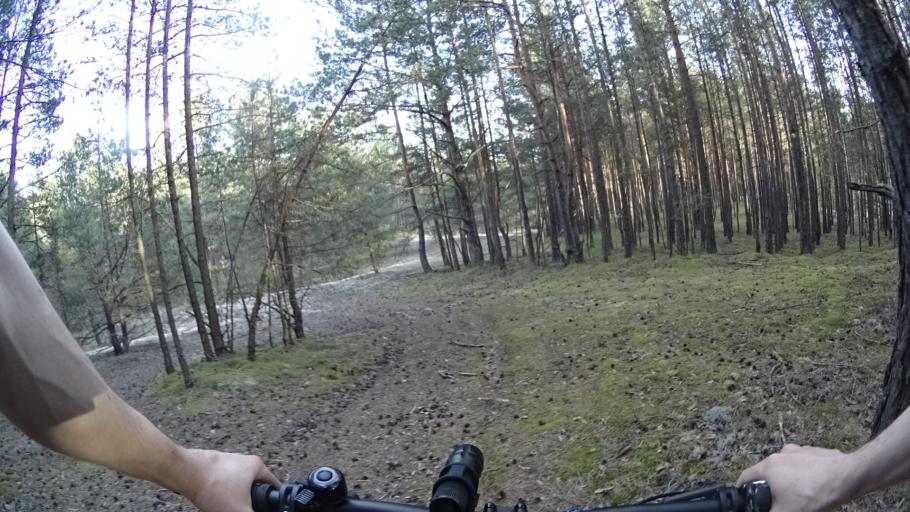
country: LV
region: Riga
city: Jaunciems
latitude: 57.1072
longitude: 24.1915
